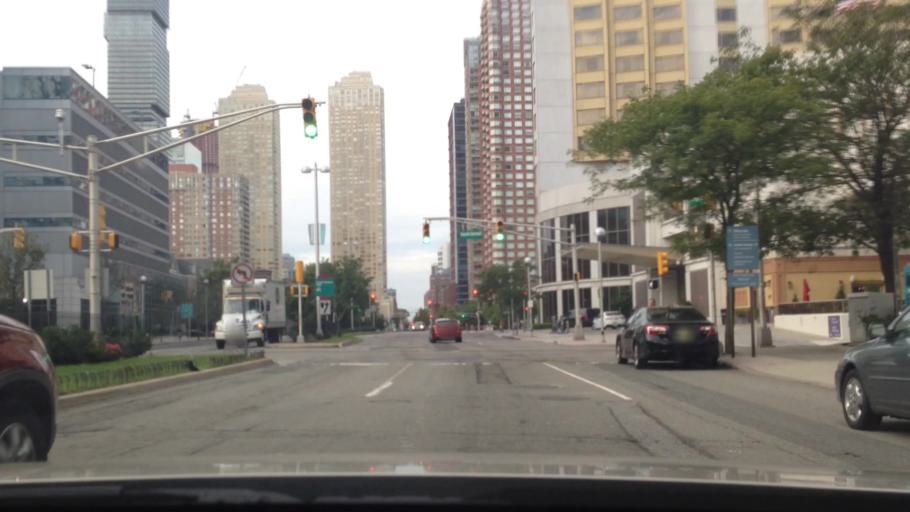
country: US
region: New Jersey
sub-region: Hudson County
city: Hoboken
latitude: 40.7256
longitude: -74.0355
